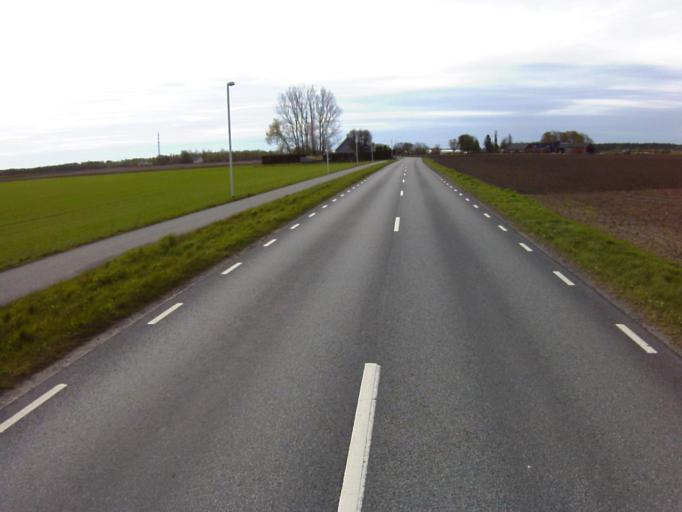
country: SE
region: Skane
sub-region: Kristianstads Kommun
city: Norra Asum
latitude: 56.0072
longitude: 14.1297
